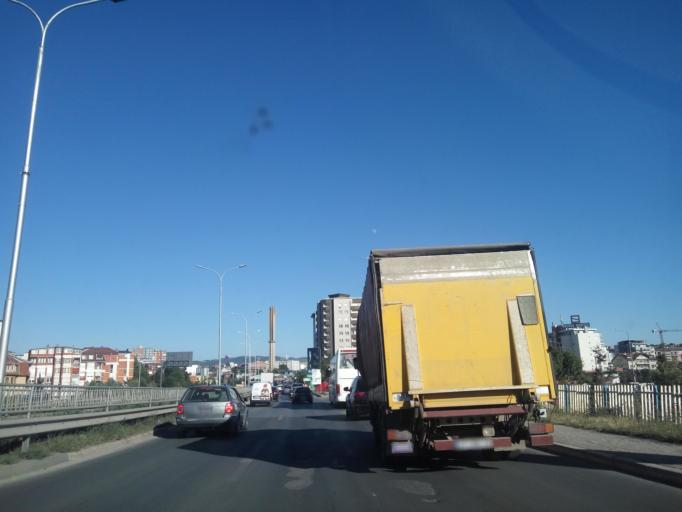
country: XK
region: Pristina
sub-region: Komuna e Prishtines
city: Pristina
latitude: 42.6511
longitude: 21.1483
